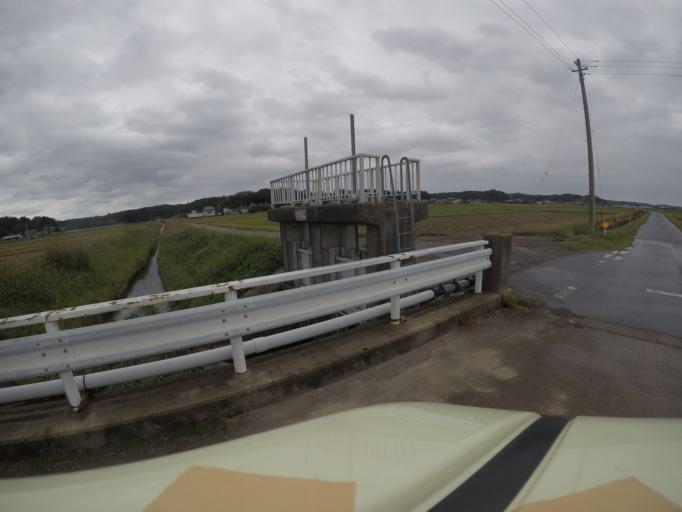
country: JP
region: Ibaraki
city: Itako
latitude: 36.0432
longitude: 140.4490
